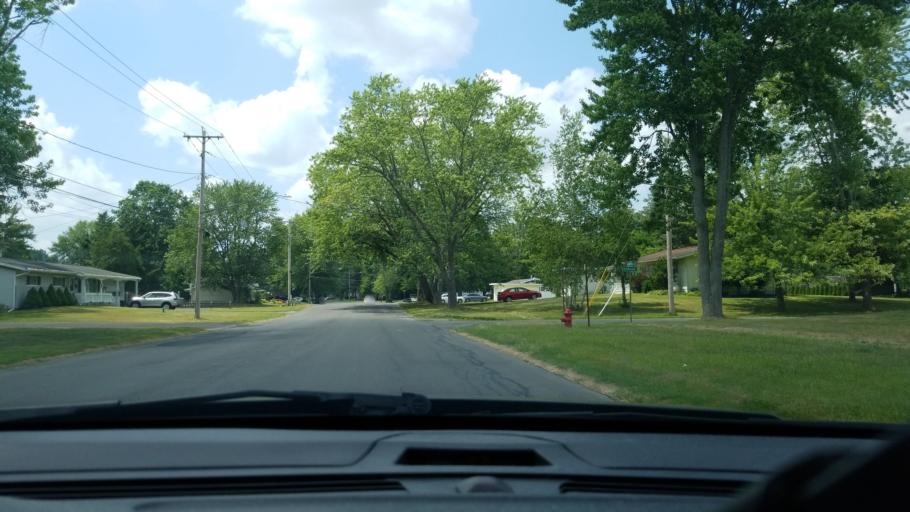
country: US
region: New York
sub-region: Onondaga County
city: Liverpool
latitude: 43.1395
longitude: -76.2194
